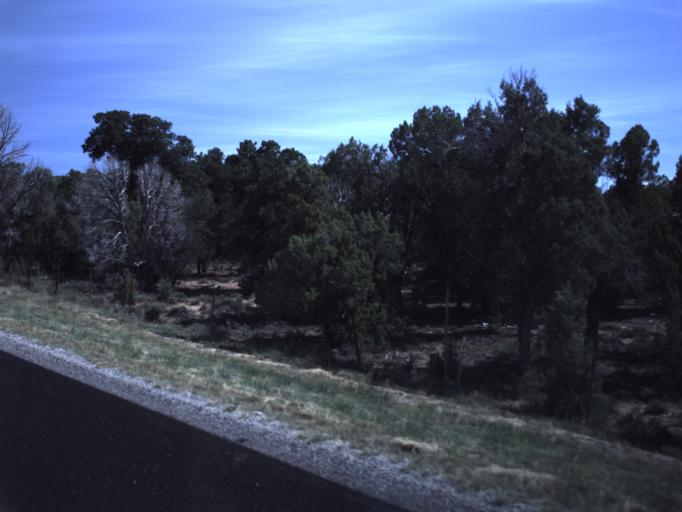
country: US
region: Utah
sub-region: San Juan County
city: Monticello
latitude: 37.8570
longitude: -109.1944
